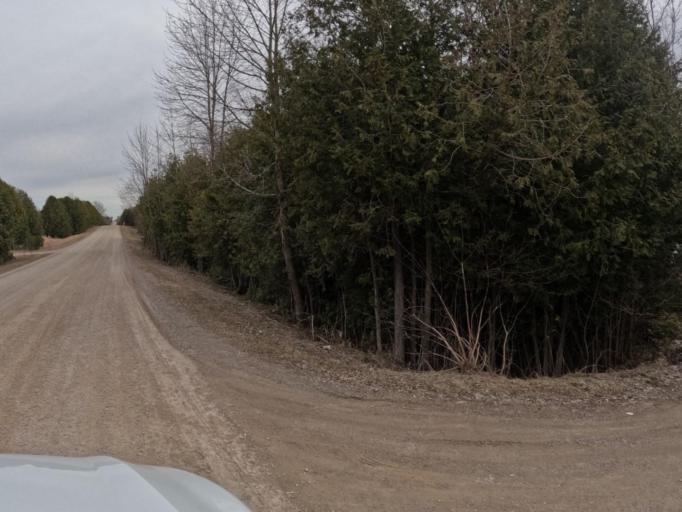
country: CA
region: Ontario
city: Orangeville
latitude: 43.9286
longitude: -80.2573
